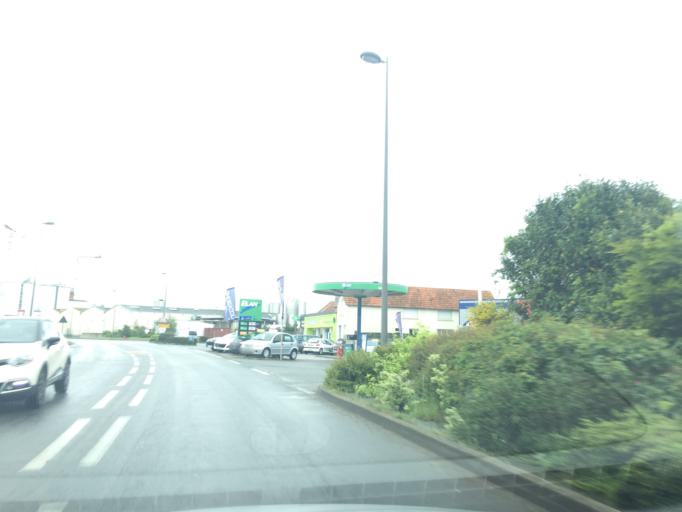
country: FR
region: Brittany
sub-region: Departement des Cotes-d'Armor
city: Crehen
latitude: 48.5433
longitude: -2.2071
